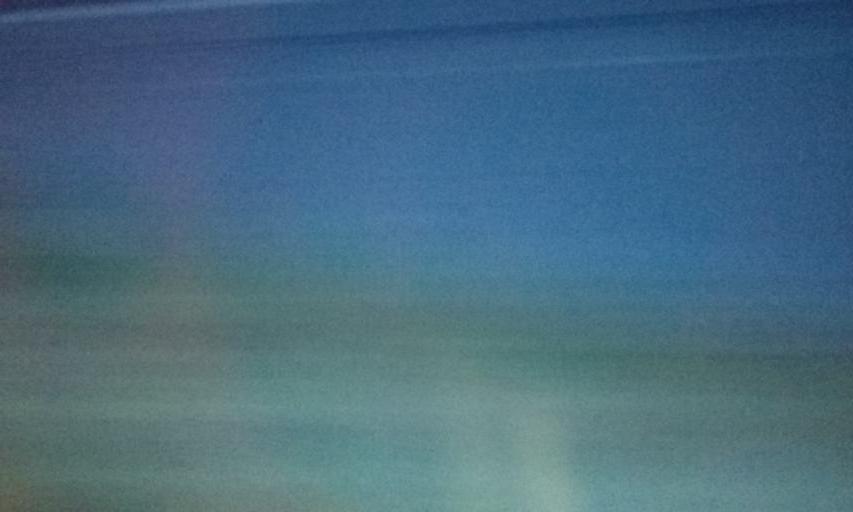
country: JP
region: Shizuoka
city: Yaizu
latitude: 34.9182
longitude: 138.3561
